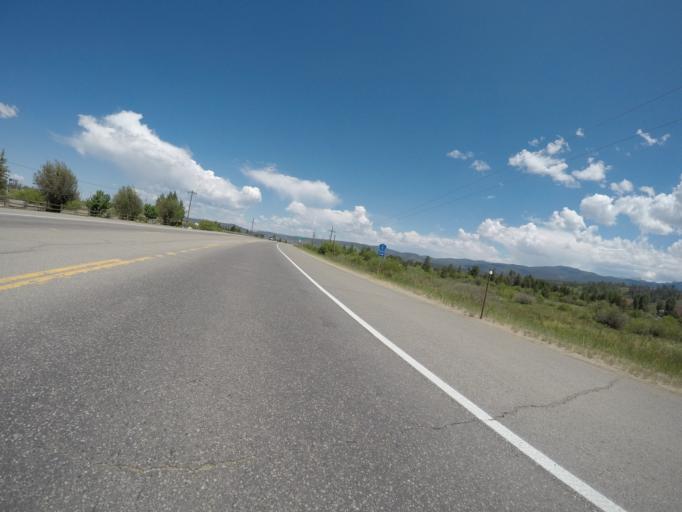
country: US
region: Colorado
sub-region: Grand County
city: Fraser
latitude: 39.9498
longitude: -105.8175
